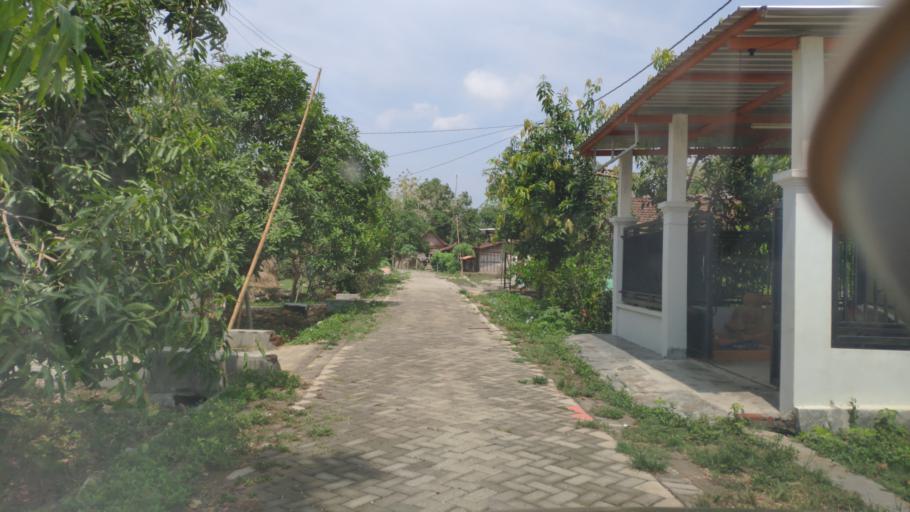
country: ID
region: Central Java
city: Karangtalun
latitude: -7.0192
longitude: 111.3580
